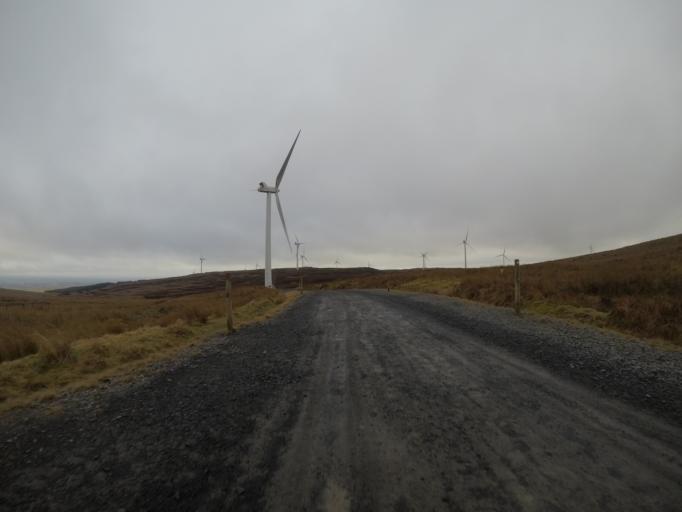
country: GB
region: Scotland
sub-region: North Ayrshire
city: Fairlie
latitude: 55.7566
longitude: -4.7953
